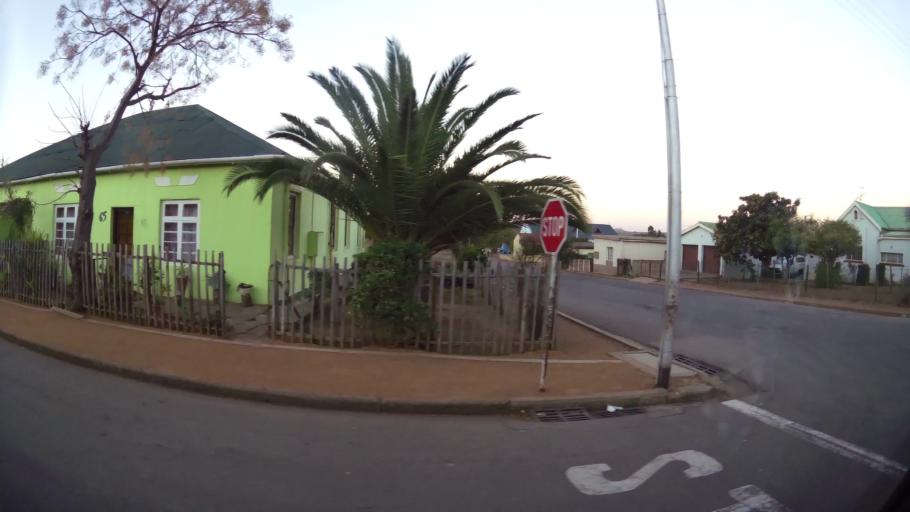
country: ZA
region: Western Cape
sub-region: Eden District Municipality
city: Riversdale
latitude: -34.0951
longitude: 21.2615
